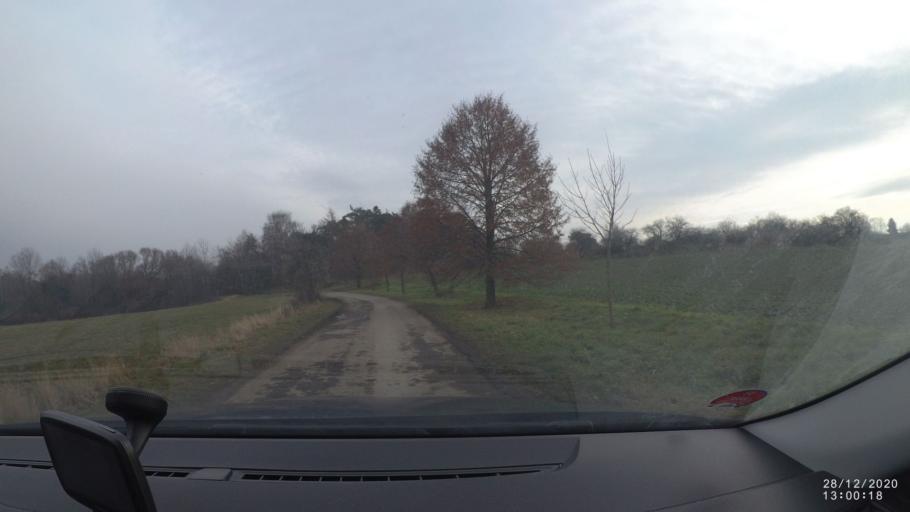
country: CZ
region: Praha
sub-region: Praha 20
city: Horni Pocernice
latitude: 50.1466
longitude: 14.6008
